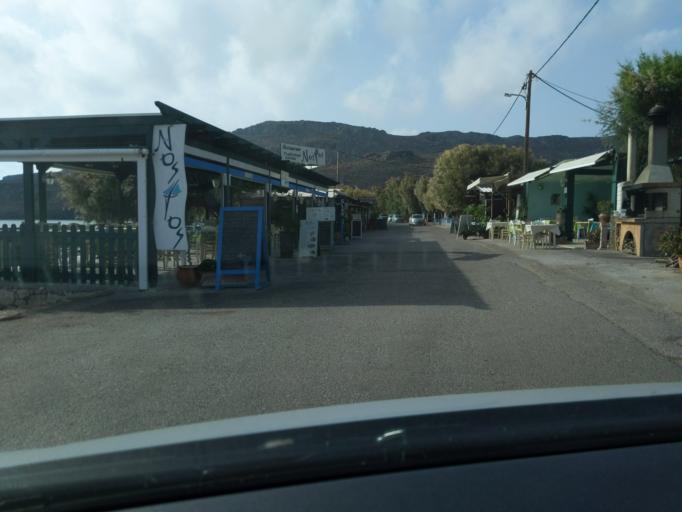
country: GR
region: Crete
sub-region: Nomos Lasithiou
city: Palekastro
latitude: 35.0978
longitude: 26.2632
